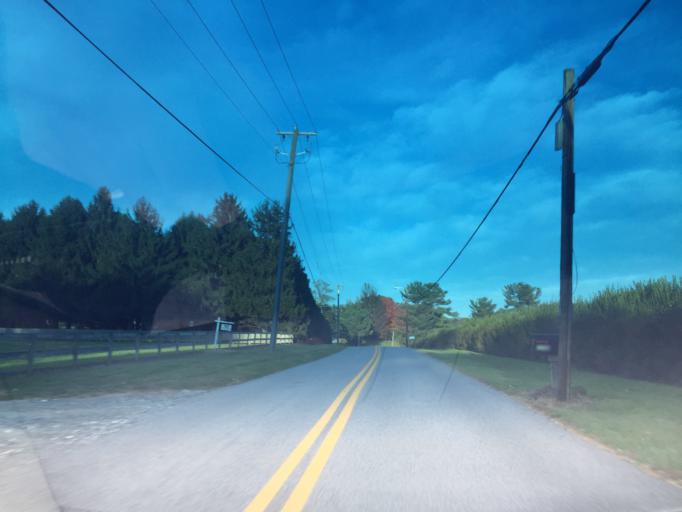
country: US
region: Maryland
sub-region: Baltimore County
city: Hampton
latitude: 39.4893
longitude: -76.5608
